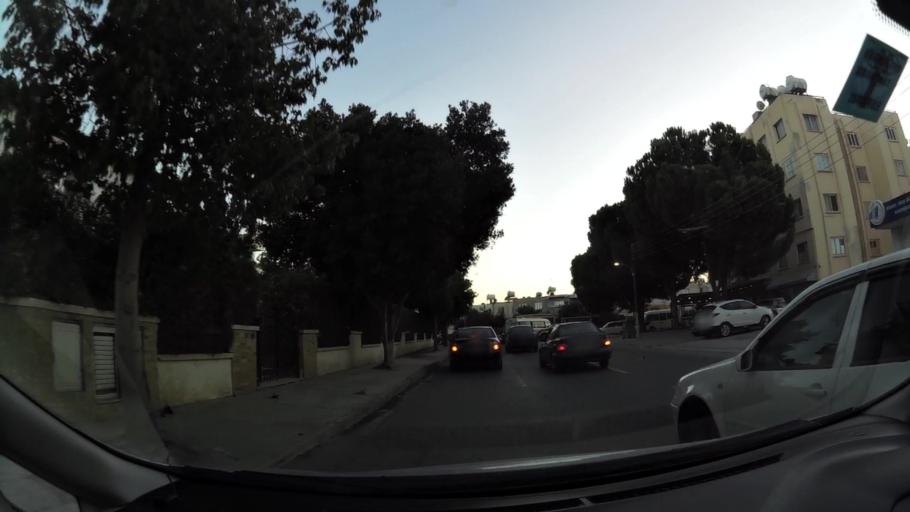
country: CY
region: Lefkosia
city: Nicosia
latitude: 35.1996
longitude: 33.3276
